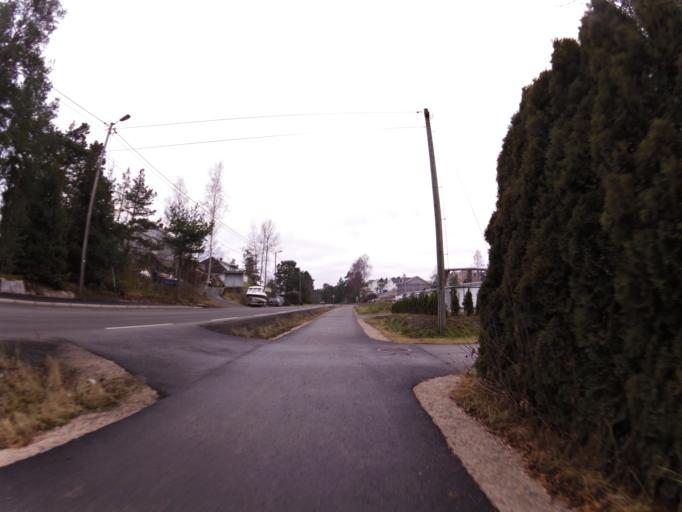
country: NO
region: Ostfold
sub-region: Fredrikstad
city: Fredrikstad
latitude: 59.1971
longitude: 10.8837
